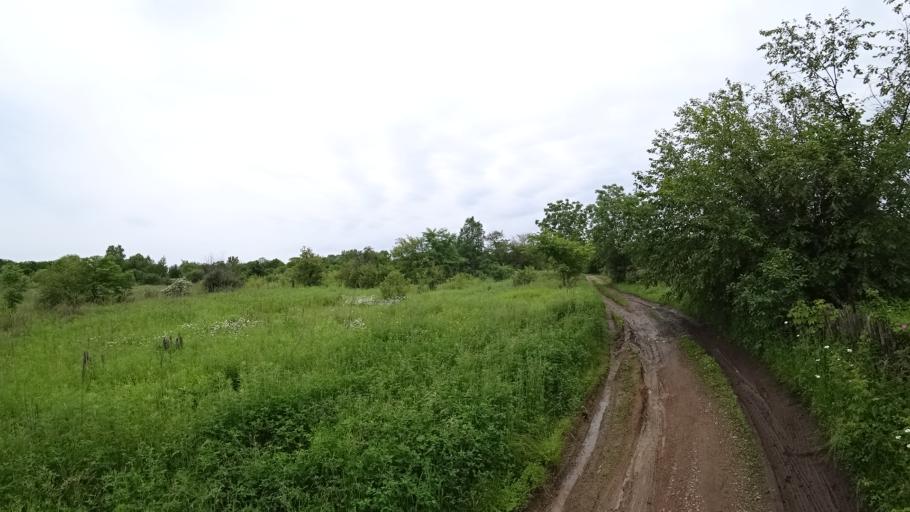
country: RU
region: Primorskiy
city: Novosysoyevka
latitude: 44.2108
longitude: 133.3269
